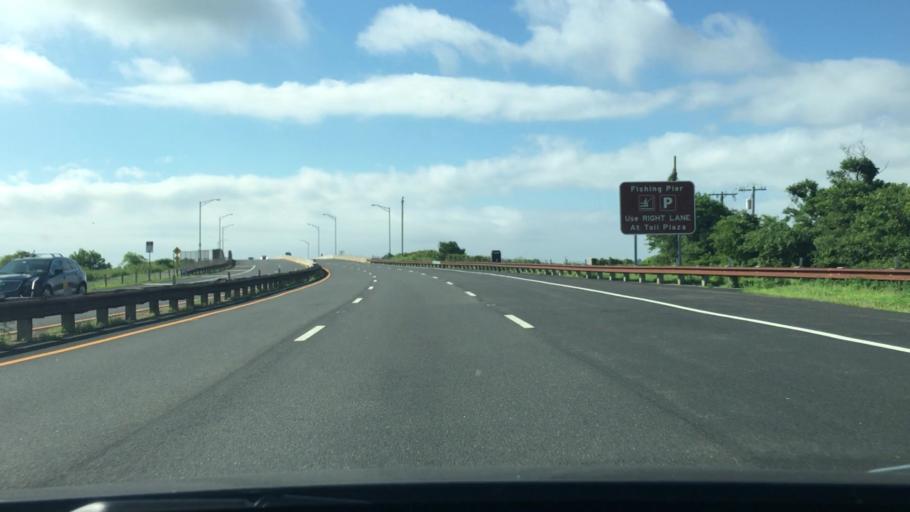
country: US
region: New York
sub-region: Nassau County
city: Seaford
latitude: 40.6255
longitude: -73.5024
